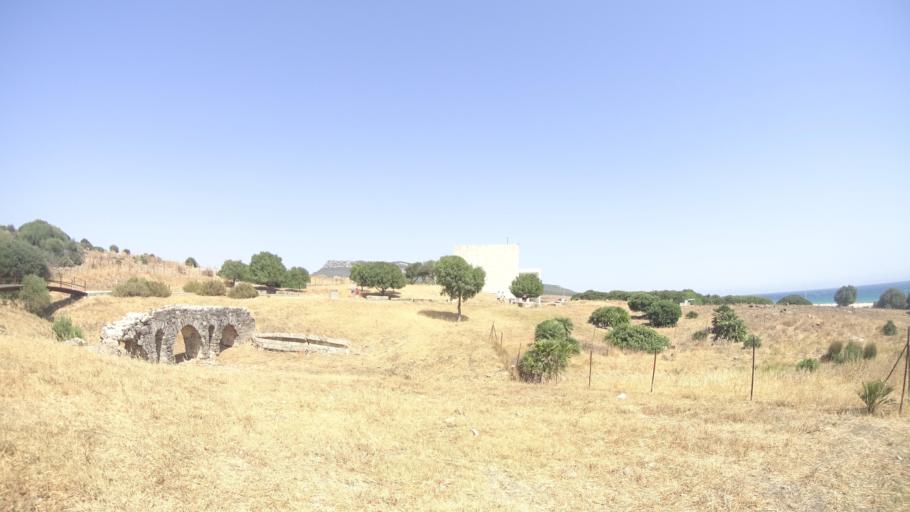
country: ES
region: Andalusia
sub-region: Provincia de Cadiz
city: Zahara de los Atunes
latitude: 36.0903
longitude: -5.7732
